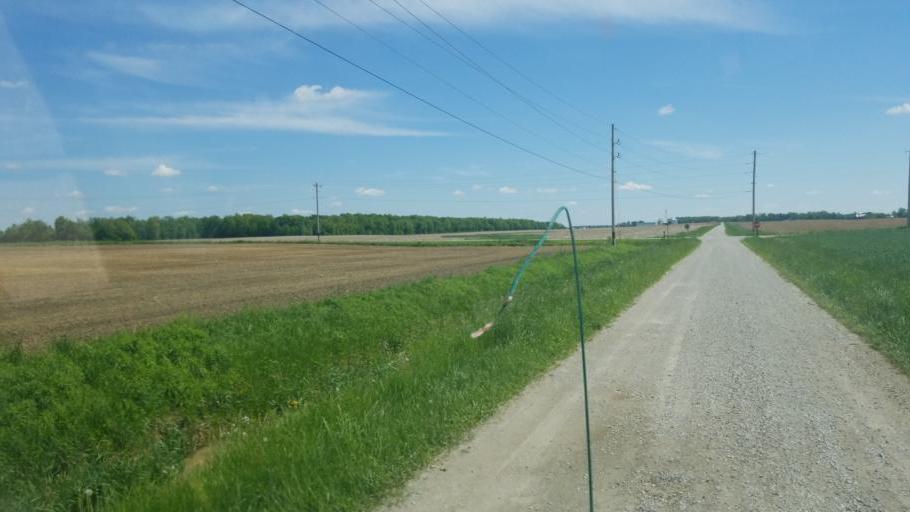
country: US
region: Ohio
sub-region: Crawford County
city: Bucyrus
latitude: 41.0091
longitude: -82.9393
